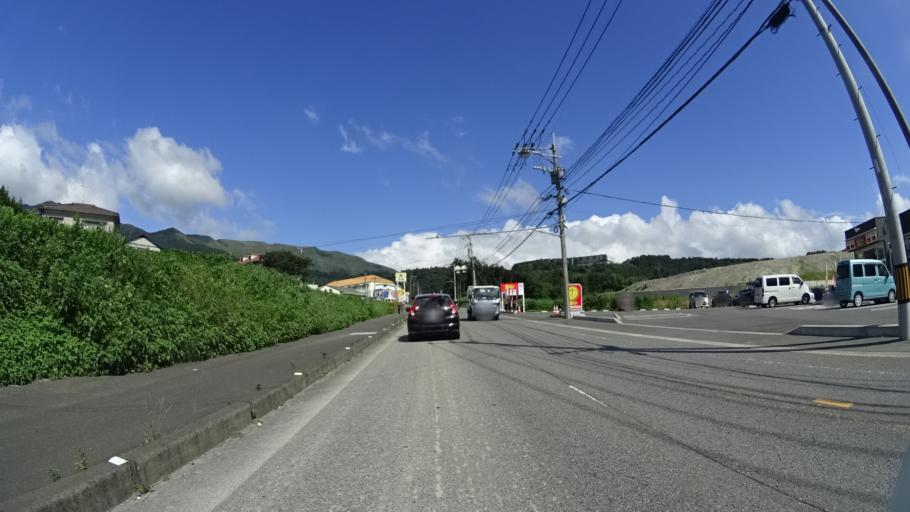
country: JP
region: Oita
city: Beppu
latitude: 33.3102
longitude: 131.4614
